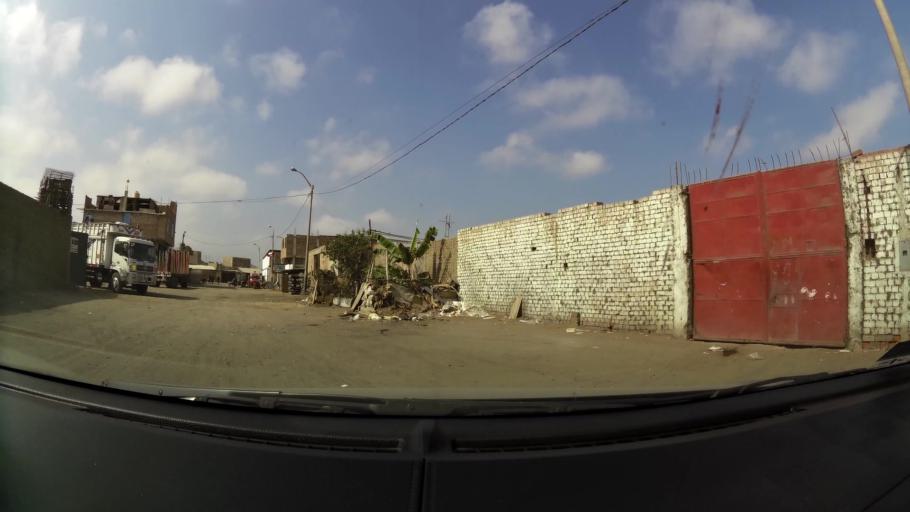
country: PE
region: La Libertad
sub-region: Provincia de Trujillo
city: Trujillo
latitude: -8.1190
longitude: -79.0149
